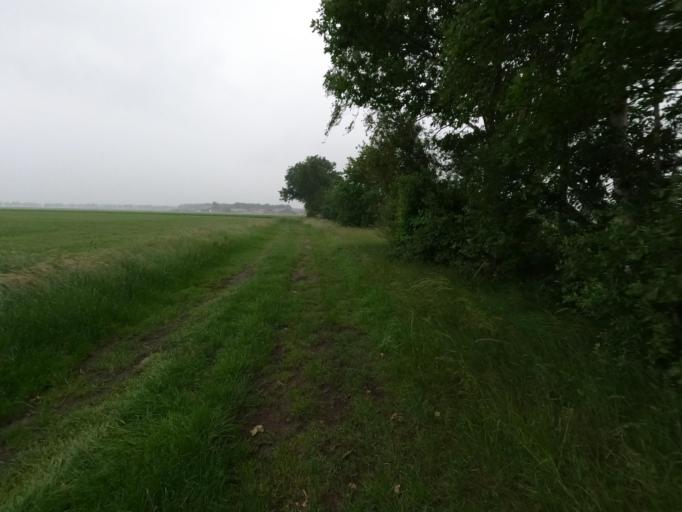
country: BE
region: Flanders
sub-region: Provincie Antwerpen
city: Kalmthout
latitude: 51.4154
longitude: 4.5162
